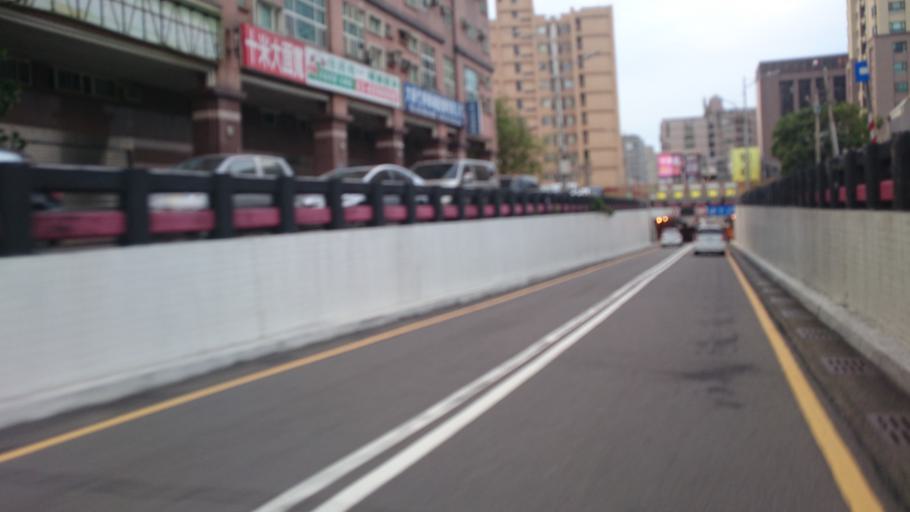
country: TW
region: Taiwan
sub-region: Hsinchu
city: Hsinchu
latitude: 24.8041
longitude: 120.9784
